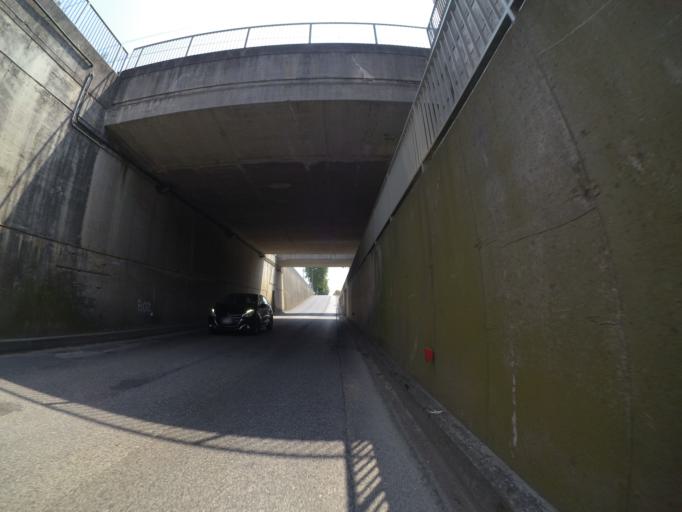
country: IT
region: Friuli Venezia Giulia
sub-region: Provincia di Udine
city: Basiliano-Vissandone
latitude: 46.0133
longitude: 13.1102
